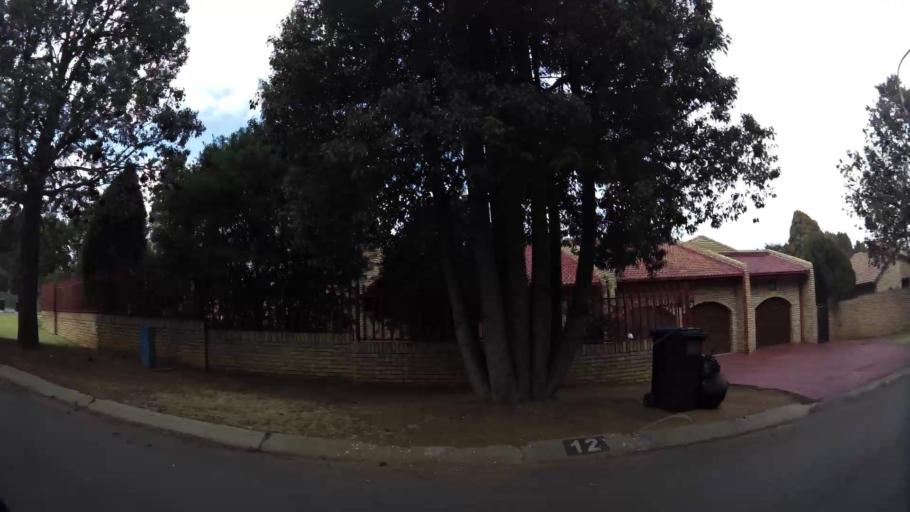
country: ZA
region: Gauteng
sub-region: Sedibeng District Municipality
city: Vanderbijlpark
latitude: -26.7399
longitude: 27.8528
